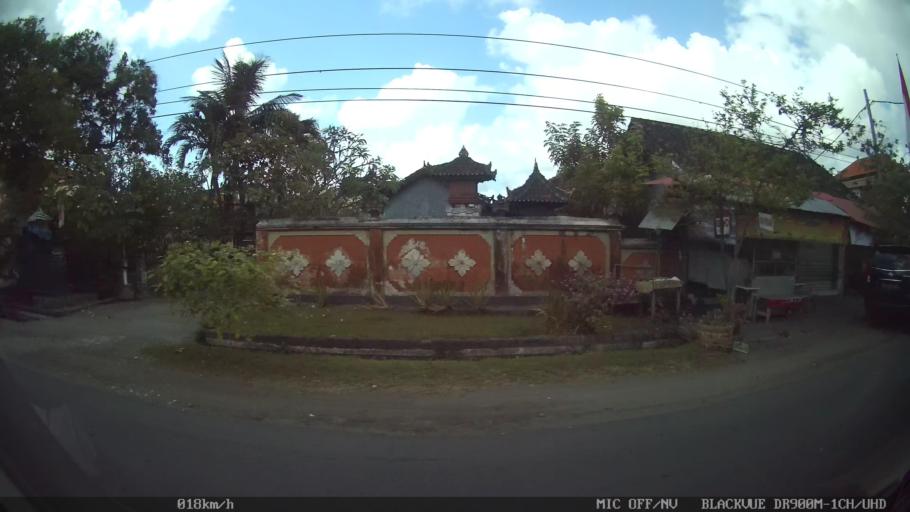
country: ID
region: Bali
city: Jabajero
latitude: -8.7203
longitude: 115.1906
